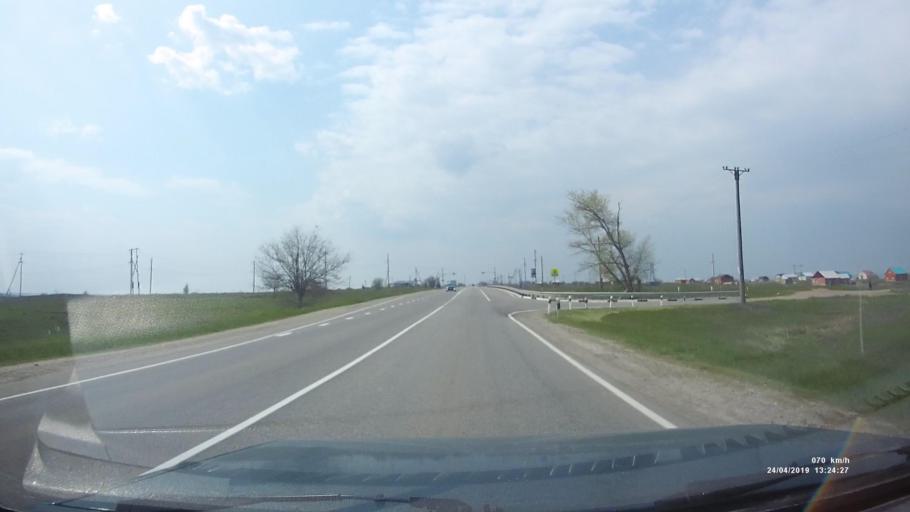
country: RU
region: Kalmykiya
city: Elista
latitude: 46.2843
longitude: 44.2546
